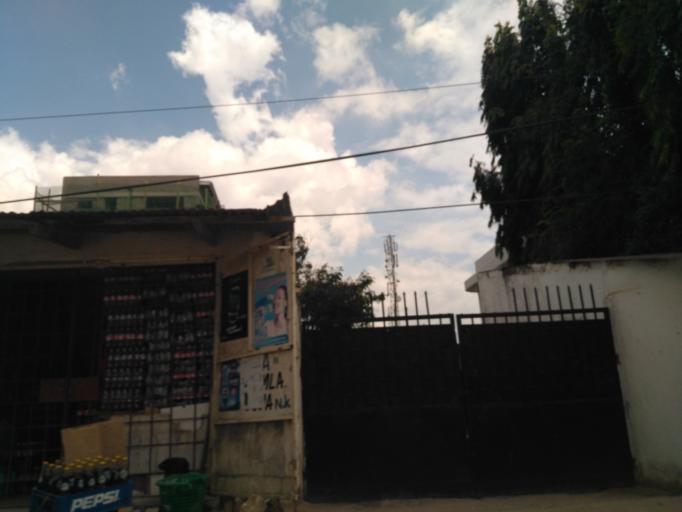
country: TZ
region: Dar es Salaam
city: Magomeni
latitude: -6.7551
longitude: 39.2411
